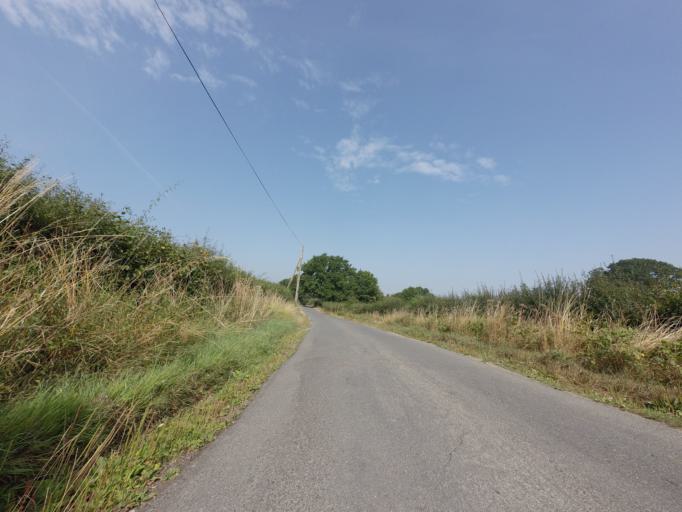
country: GB
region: England
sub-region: Kent
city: Headcorn
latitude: 51.1197
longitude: 0.6058
